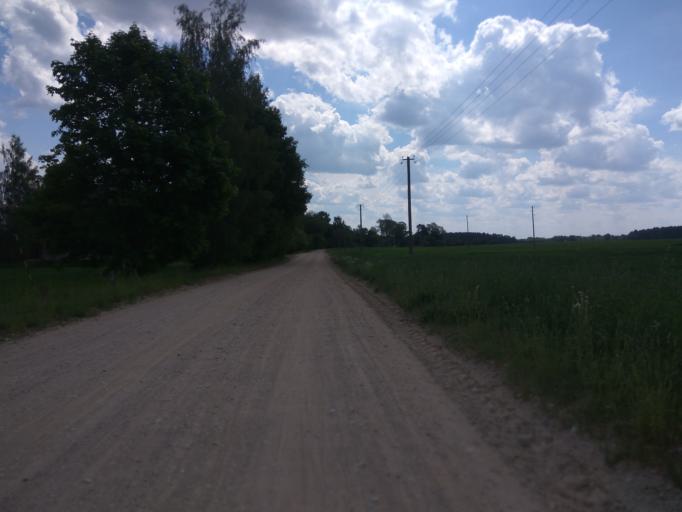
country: LV
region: Kuldigas Rajons
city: Kuldiga
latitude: 56.8941
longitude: 21.9696
